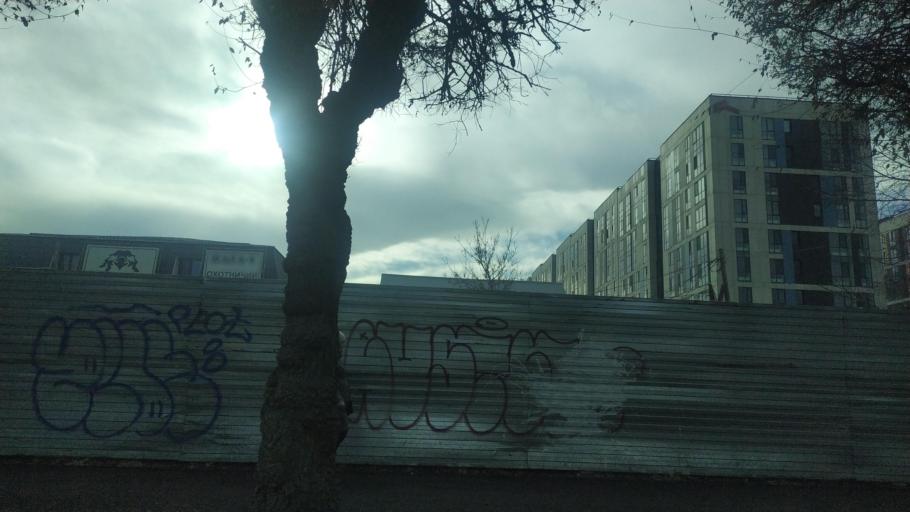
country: KZ
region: Almaty Qalasy
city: Almaty
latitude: 43.2381
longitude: 76.8891
